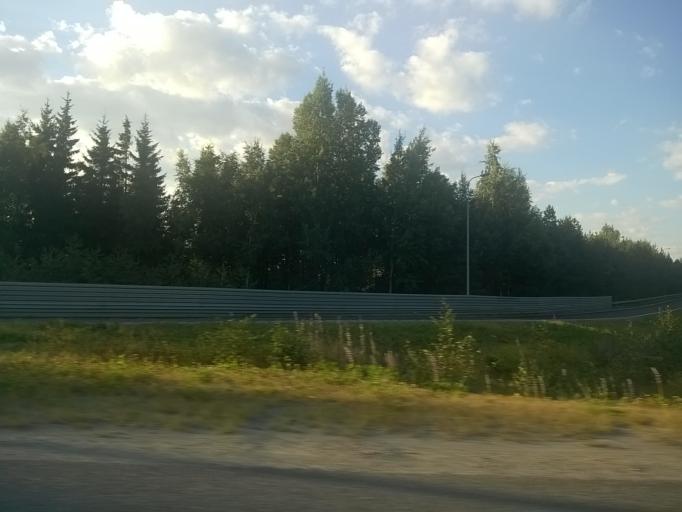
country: FI
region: Pirkanmaa
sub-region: Tampere
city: Tampere
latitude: 61.4626
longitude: 23.7607
